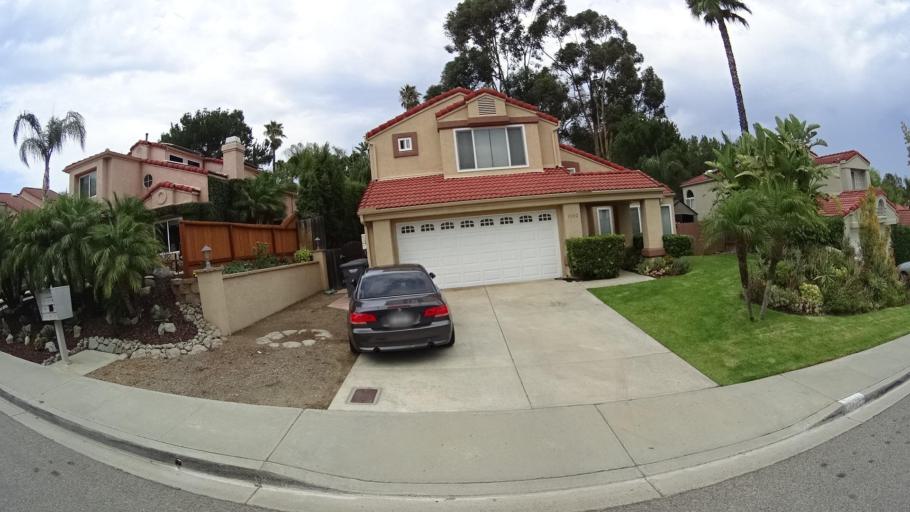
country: US
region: California
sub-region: San Diego County
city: Escondido
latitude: 33.1320
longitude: -117.1106
